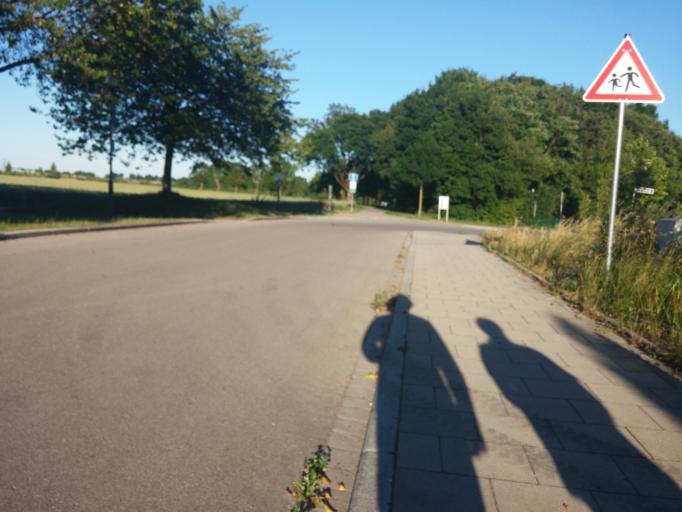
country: DE
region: Bavaria
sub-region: Upper Bavaria
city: Aschheim
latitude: 48.1680
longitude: 11.7243
